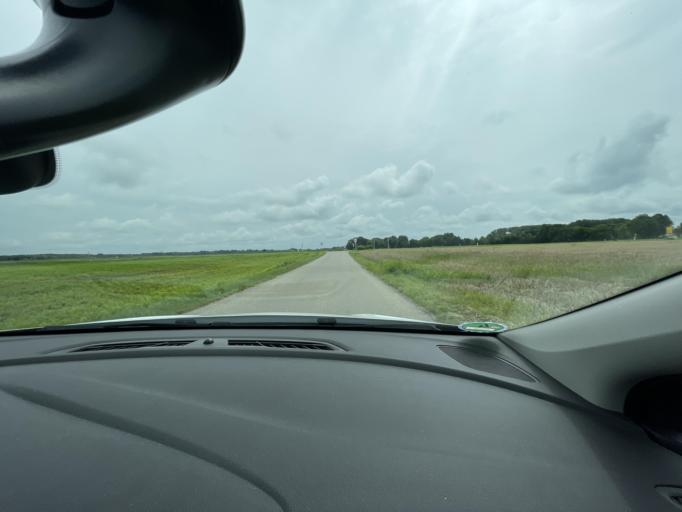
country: DE
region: Bavaria
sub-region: Swabia
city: Nordendorf
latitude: 48.5959
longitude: 10.8450
